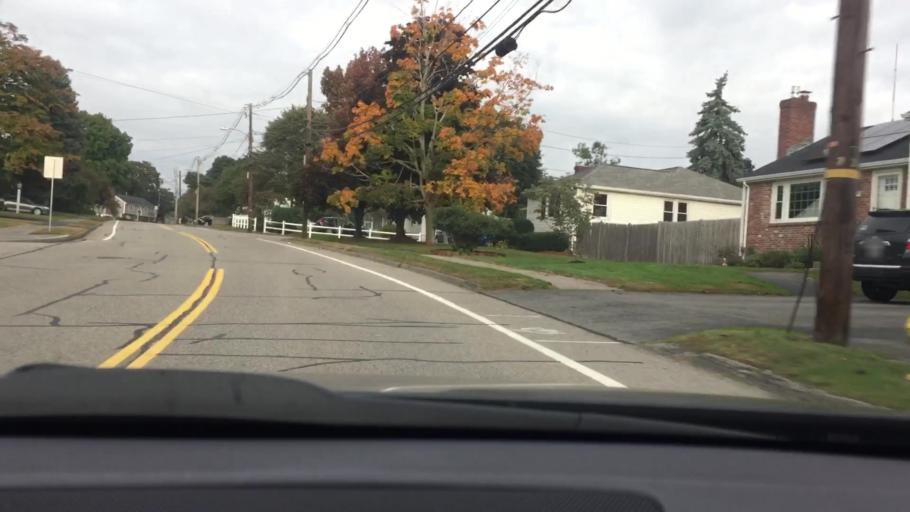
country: US
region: Massachusetts
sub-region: Norfolk County
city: Needham
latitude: 42.2991
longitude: -71.2250
